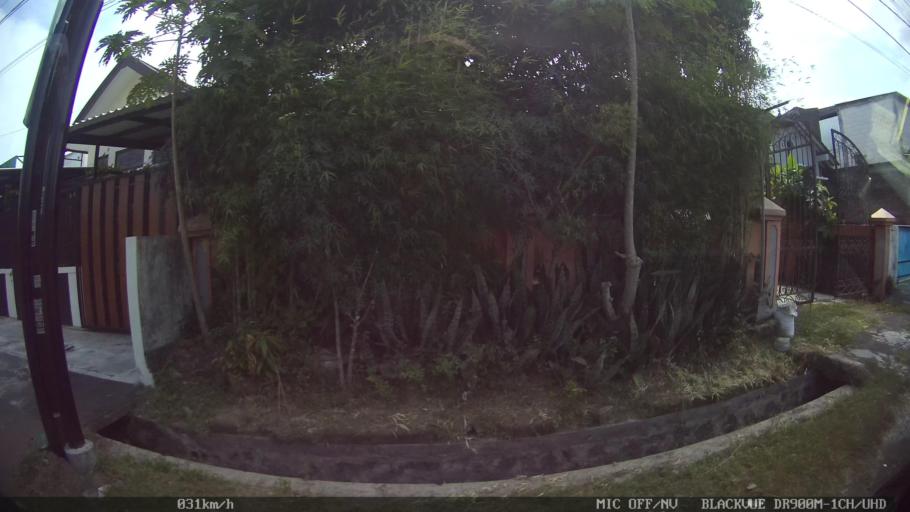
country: ID
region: Daerah Istimewa Yogyakarta
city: Depok
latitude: -7.7680
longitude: 110.4389
